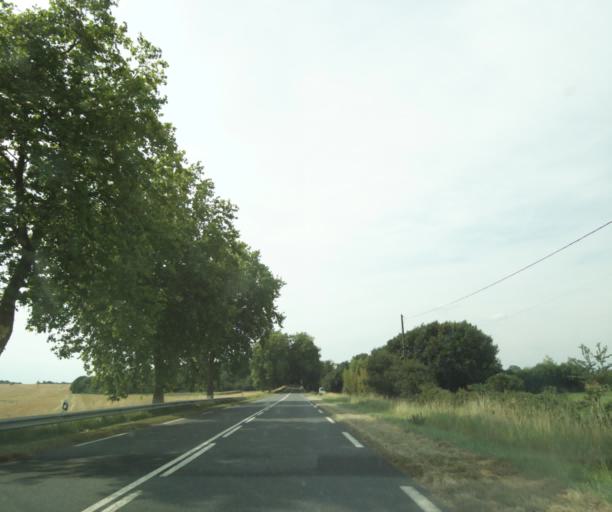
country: FR
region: Centre
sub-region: Departement d'Indre-et-Loire
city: Saint-Paterne-Racan
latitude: 47.6099
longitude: 0.5107
